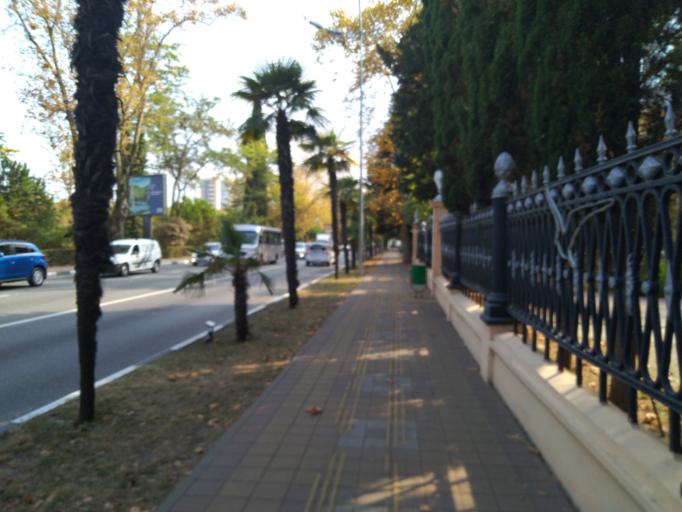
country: RU
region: Krasnodarskiy
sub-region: Sochi City
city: Sochi
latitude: 43.5920
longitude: 39.7173
